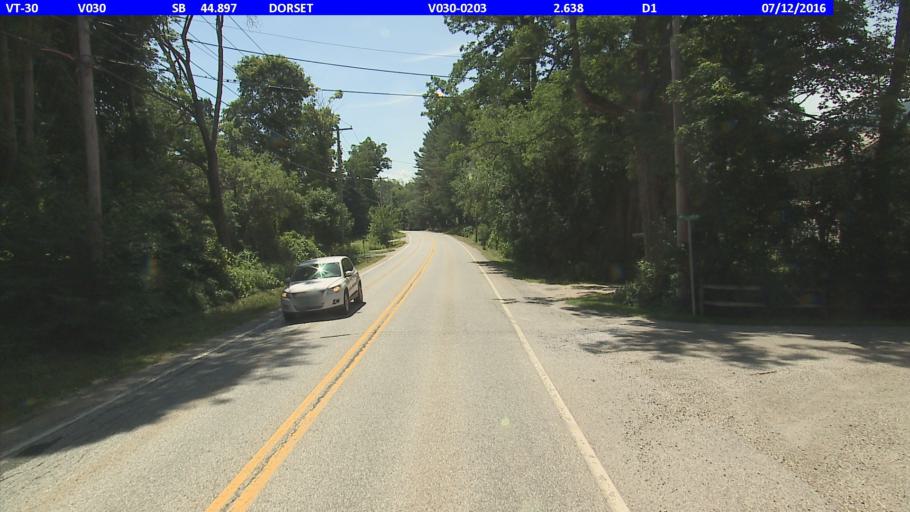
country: US
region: Vermont
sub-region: Bennington County
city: Manchester Center
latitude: 43.2459
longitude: -73.0916
